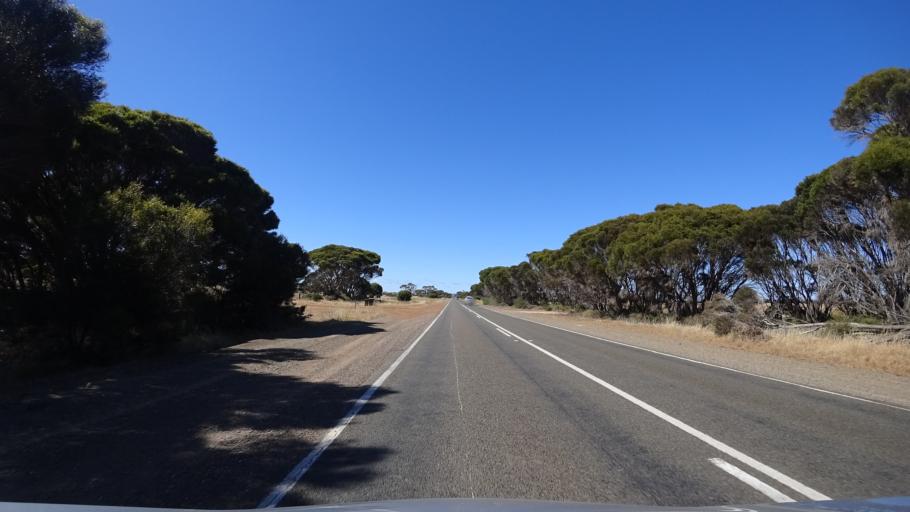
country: AU
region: South Australia
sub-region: Kangaroo Island
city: Kingscote
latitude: -35.6863
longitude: 137.5724
